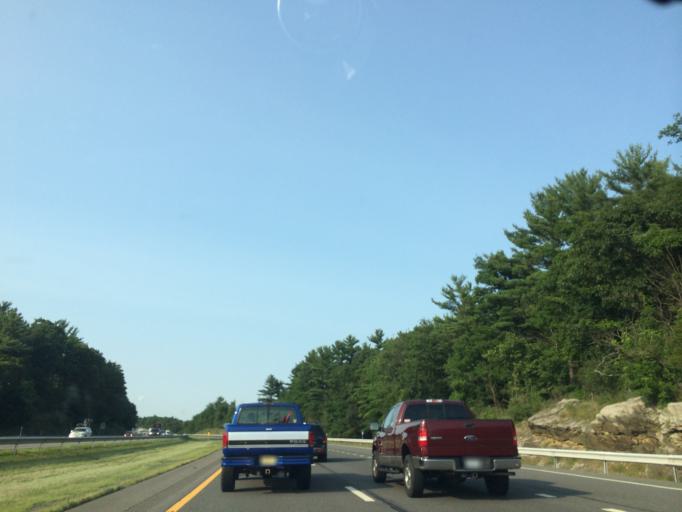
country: US
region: New York
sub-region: Greene County
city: Jefferson Heights
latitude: 42.2521
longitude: -73.8822
